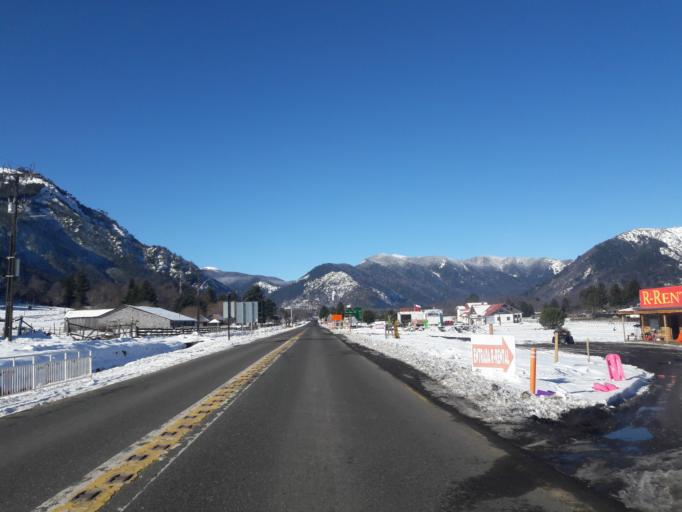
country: CL
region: Araucania
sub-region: Provincia de Cautin
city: Vilcun
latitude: -38.4712
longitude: -71.5762
